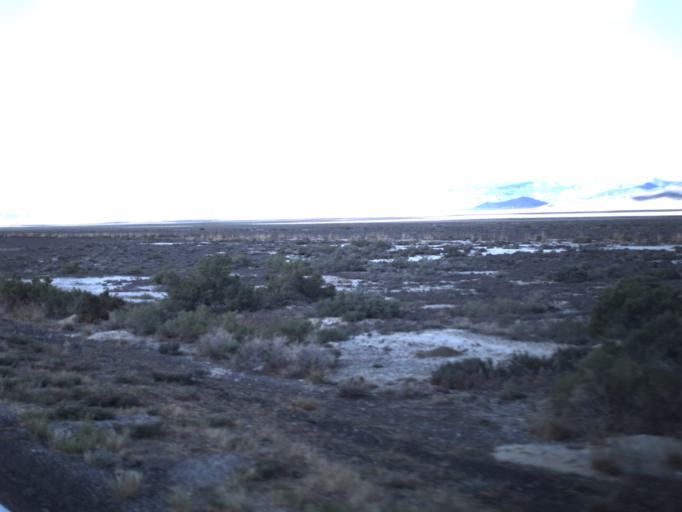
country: US
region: Utah
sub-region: Millard County
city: Delta
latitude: 39.0369
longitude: -112.7729
